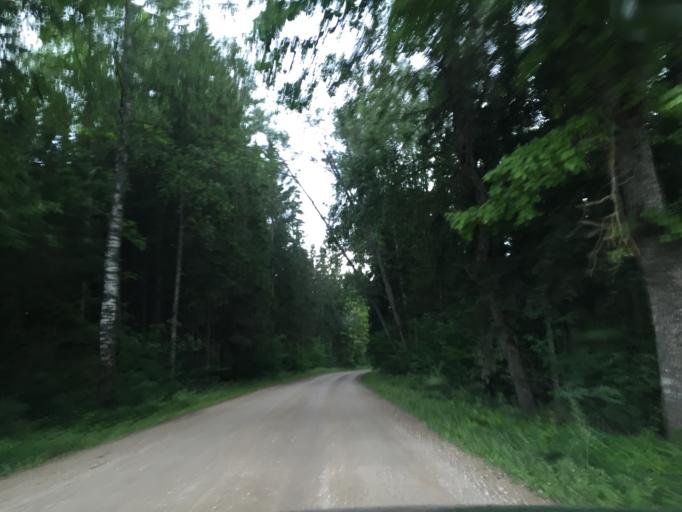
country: LV
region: Malpils
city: Malpils
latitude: 56.9405
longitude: 25.0066
